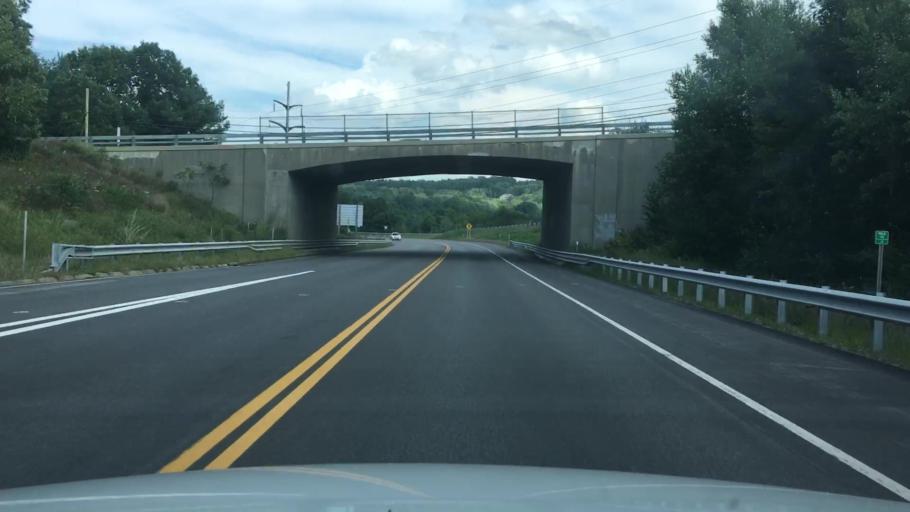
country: US
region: New Hampshire
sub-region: Belknap County
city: Laconia
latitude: 43.5123
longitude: -71.4596
